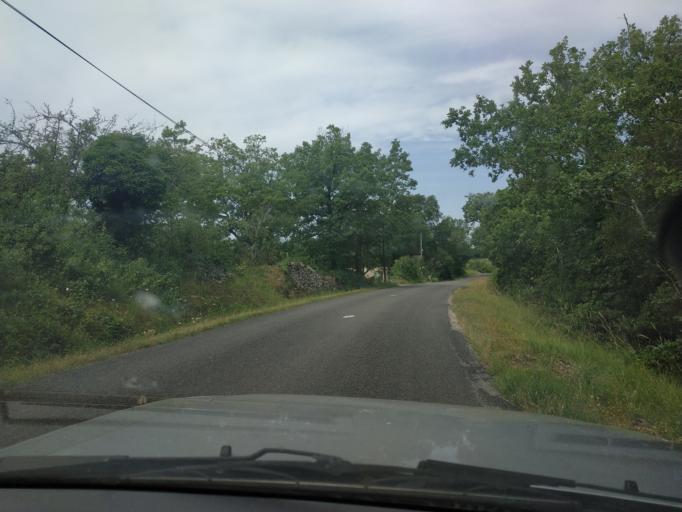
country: FR
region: Midi-Pyrenees
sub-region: Departement du Lot
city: Gramat
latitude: 44.6086
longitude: 1.6363
